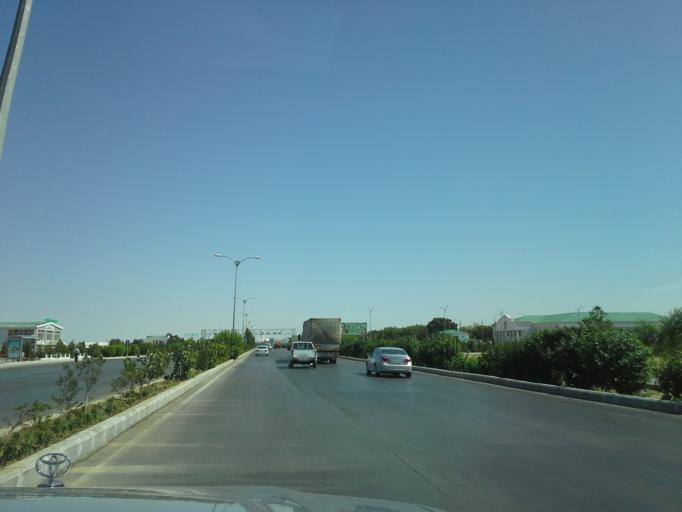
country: TM
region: Ahal
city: Annau
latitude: 37.9099
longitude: 58.5024
